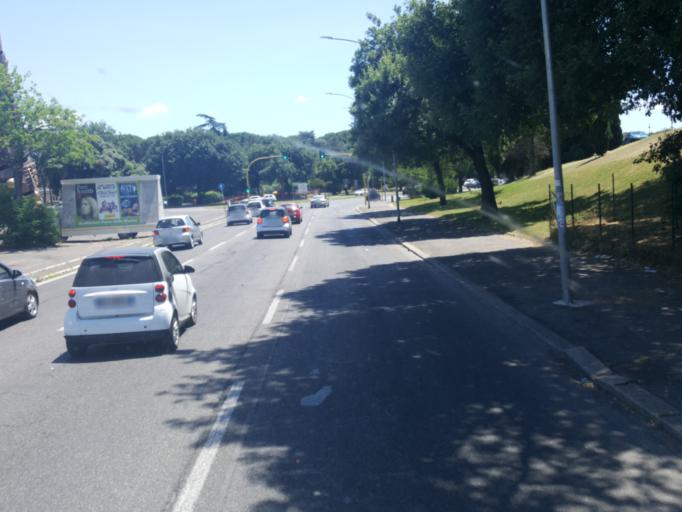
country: IT
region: Latium
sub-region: Citta metropolitana di Roma Capitale
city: Selcetta
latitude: 41.8235
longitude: 12.4646
